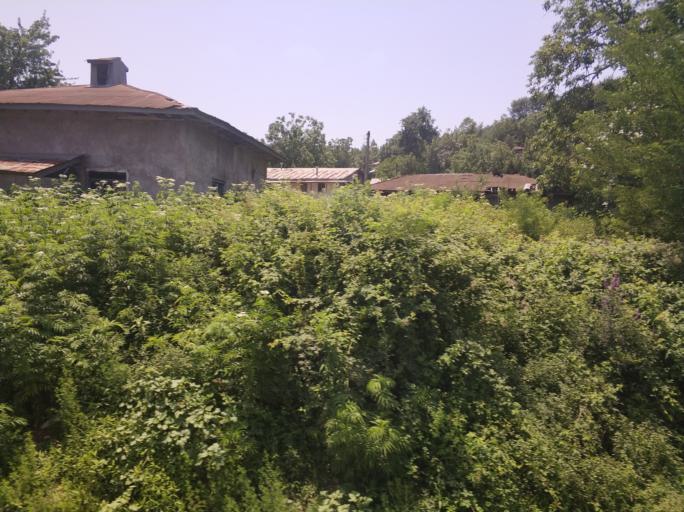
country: IR
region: Gilan
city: Pa'in-e Bazar-e Rudbar
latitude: 37.0066
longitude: 49.5965
